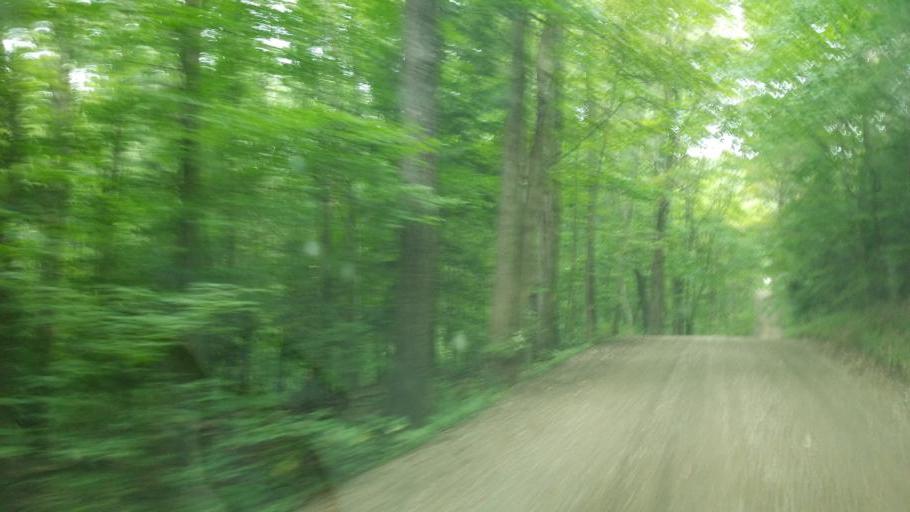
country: US
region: Ohio
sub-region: Ashland County
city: Loudonville
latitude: 40.5913
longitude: -82.2978
